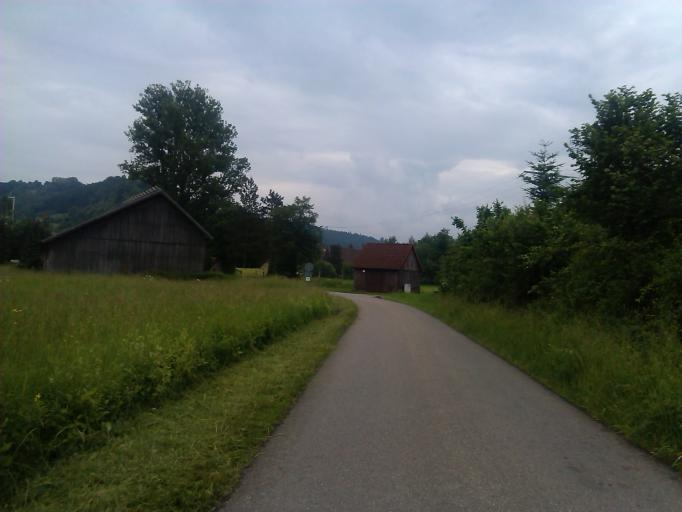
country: DE
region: Baden-Wuerttemberg
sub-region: Regierungsbezirk Stuttgart
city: Oberrot
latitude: 49.0036
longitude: 9.6745
